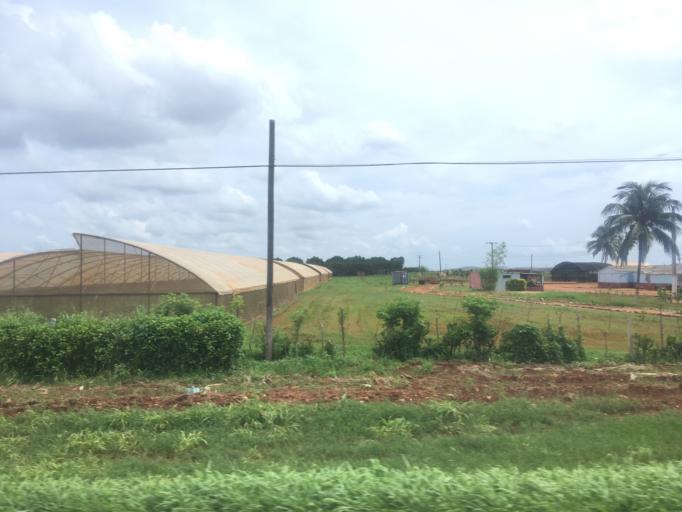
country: CU
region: Matanzas
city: Jovellanos
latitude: 22.7983
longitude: -81.1623
